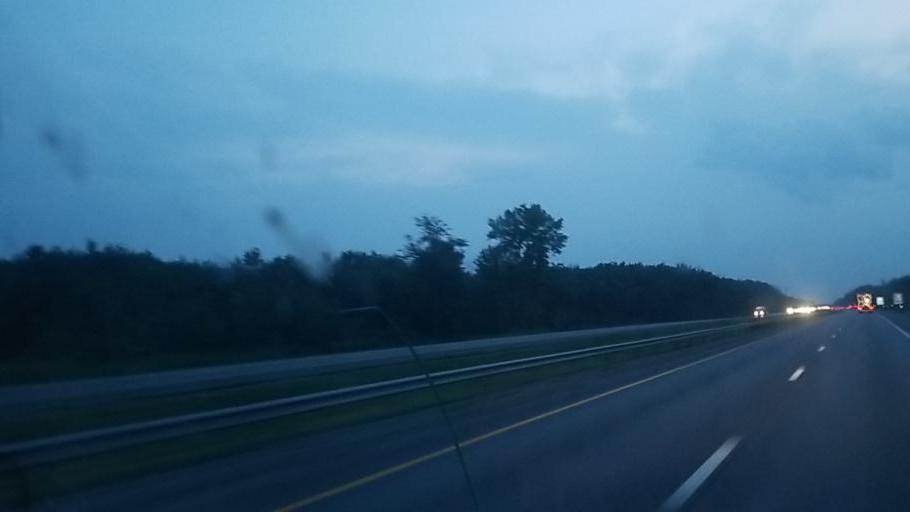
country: US
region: New York
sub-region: Onondaga County
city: Minoa
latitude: 43.0940
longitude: -75.9844
